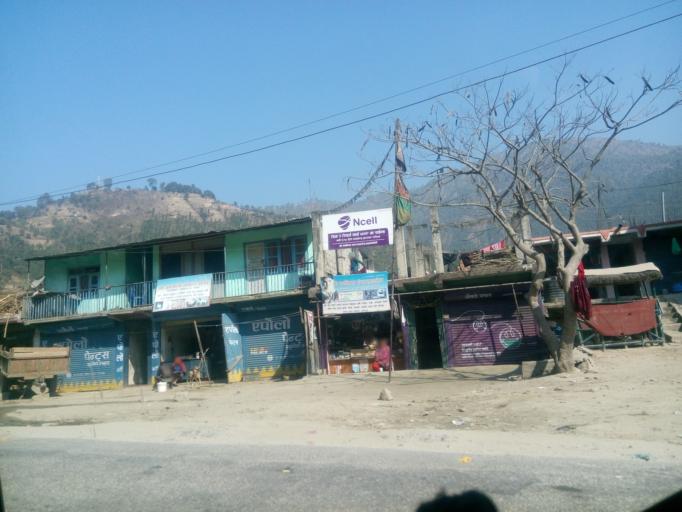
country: NP
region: Central Region
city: Kirtipur
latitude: 27.7533
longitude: 85.0634
